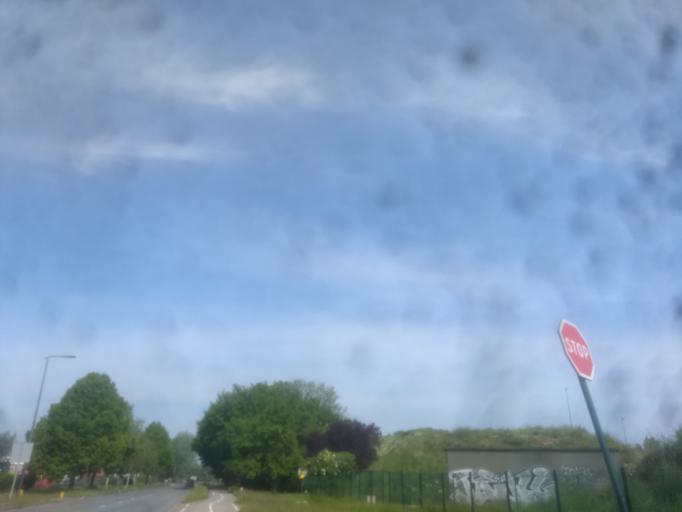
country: FR
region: Nord-Pas-de-Calais
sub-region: Departement du Pas-de-Calais
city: Tilloy-les-Mofflaines
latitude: 50.2849
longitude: 2.8117
